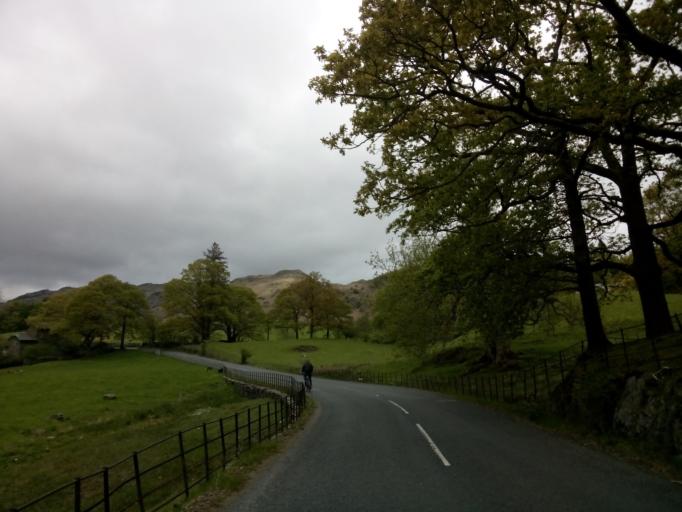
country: GB
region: England
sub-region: Cumbria
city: Ambleside
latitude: 54.4320
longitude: -3.0253
